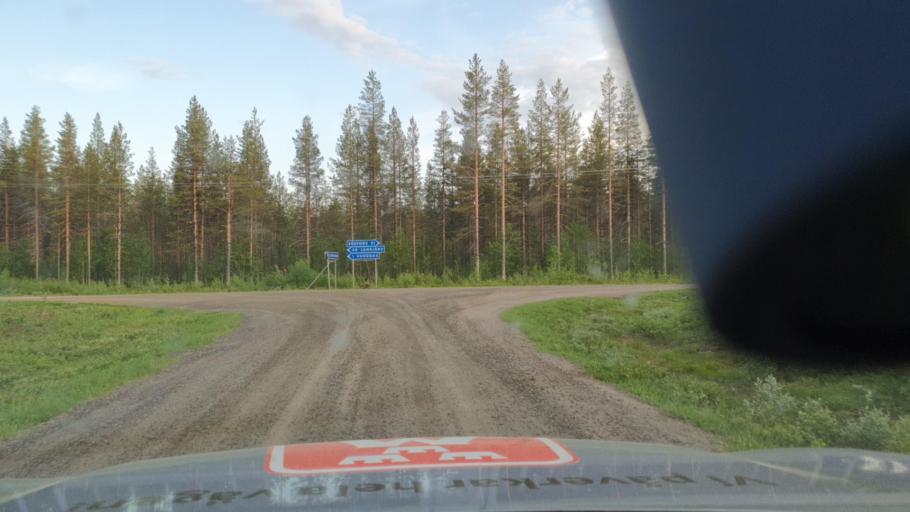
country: SE
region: Norrbotten
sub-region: Bodens Kommun
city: Boden
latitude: 66.4212
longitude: 21.7148
